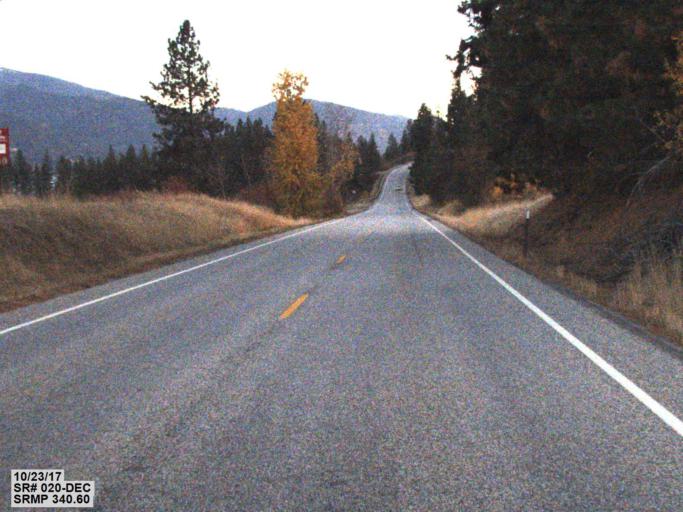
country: US
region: Washington
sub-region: Stevens County
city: Kettle Falls
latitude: 48.6106
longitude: -118.1384
